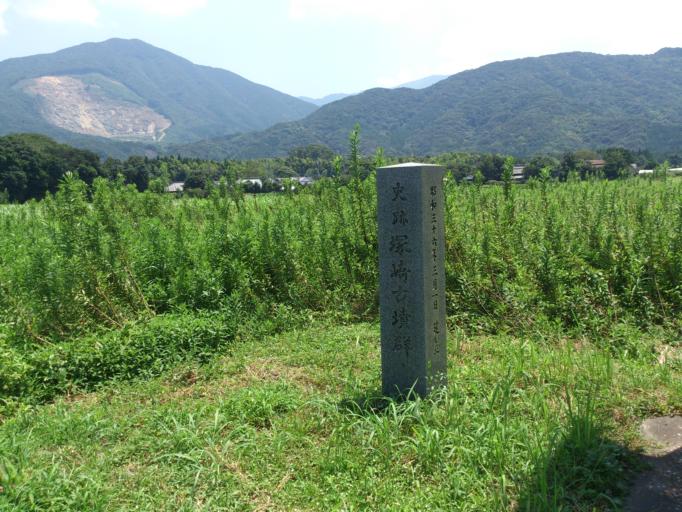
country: JP
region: Kagoshima
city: Kanoya
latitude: 31.3423
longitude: 130.9686
